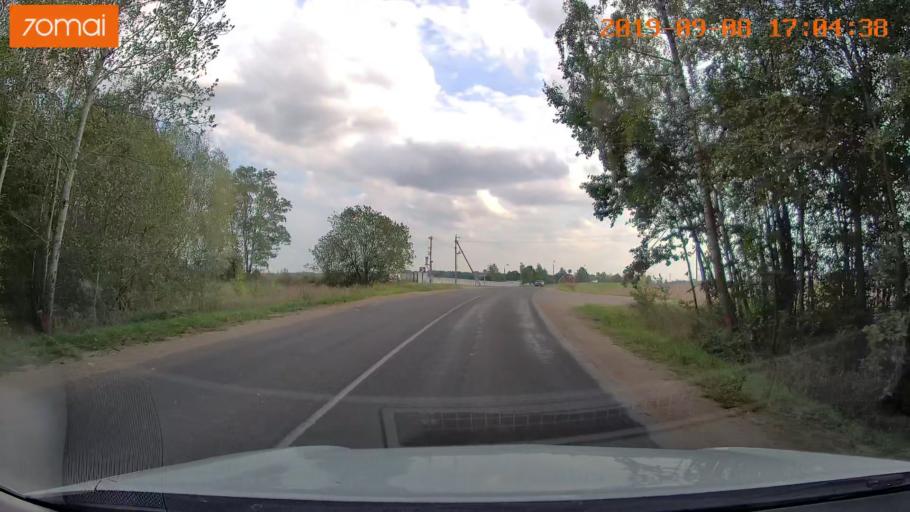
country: BY
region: Grodnenskaya
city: Hrodna
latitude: 53.6879
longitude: 23.9550
